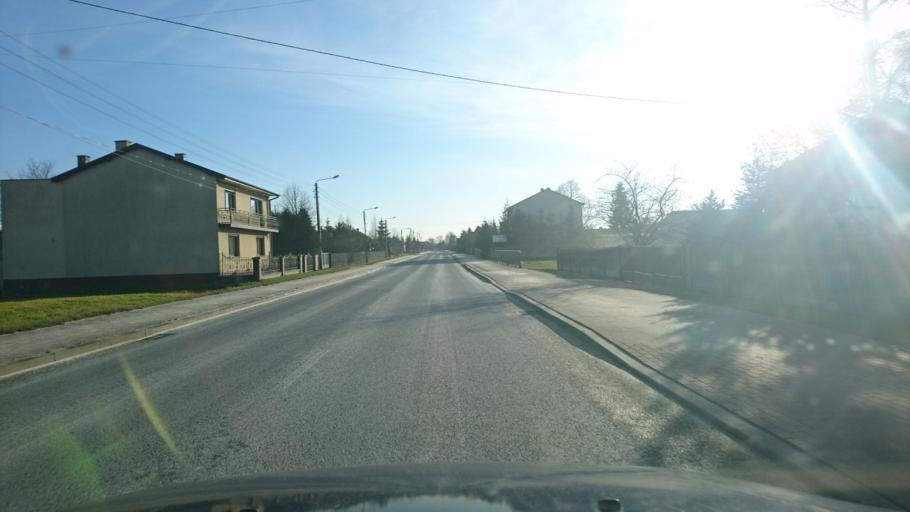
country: PL
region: Silesian Voivodeship
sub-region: Powiat klobucki
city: Starokrzepice
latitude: 51.0087
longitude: 18.6576
